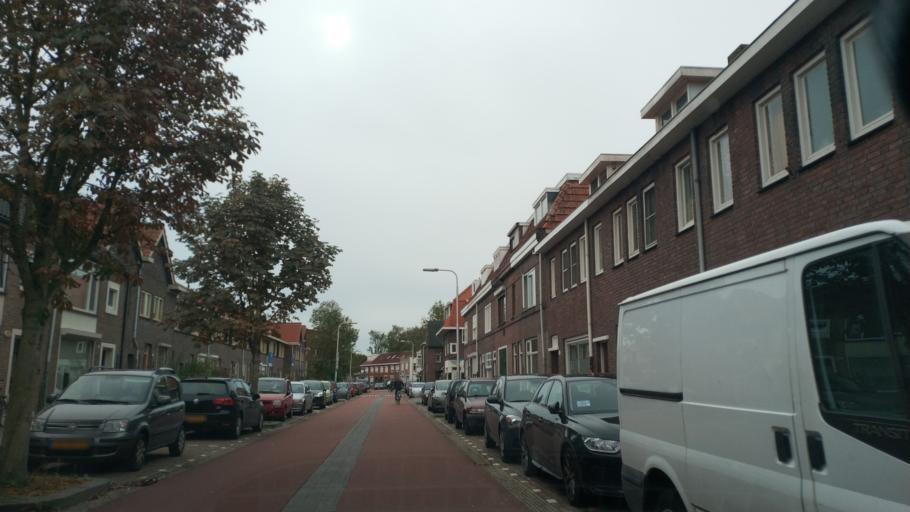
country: NL
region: North Brabant
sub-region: Gemeente Tilburg
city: Tilburg
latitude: 51.5505
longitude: 5.0779
